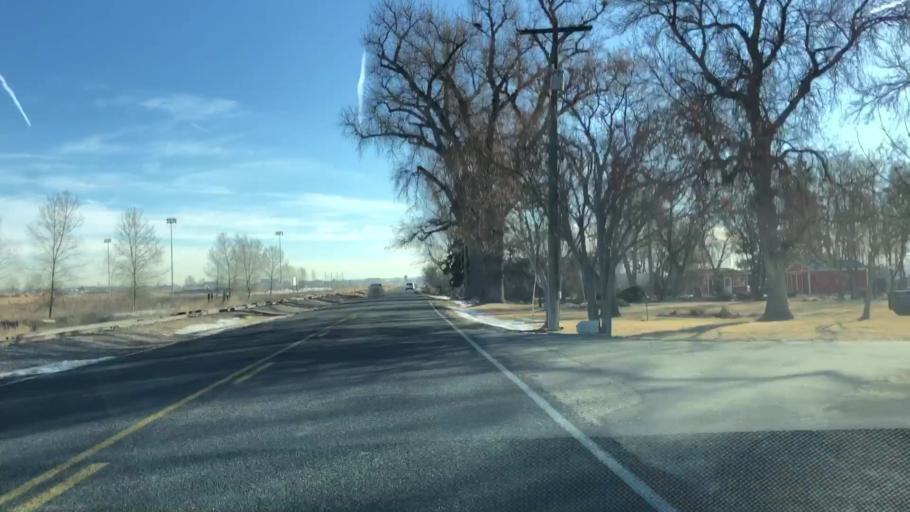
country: US
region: Colorado
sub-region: Larimer County
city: Loveland
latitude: 40.3999
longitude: -105.0187
